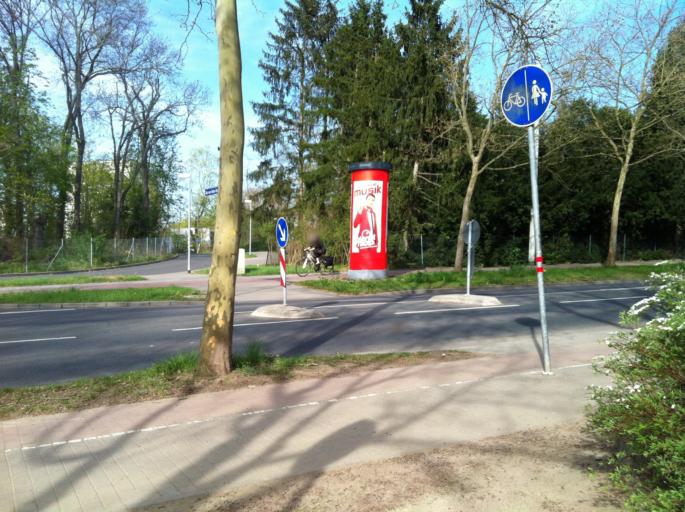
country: DE
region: Rheinland-Pfalz
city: Mainz
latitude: 49.9988
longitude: 8.2367
